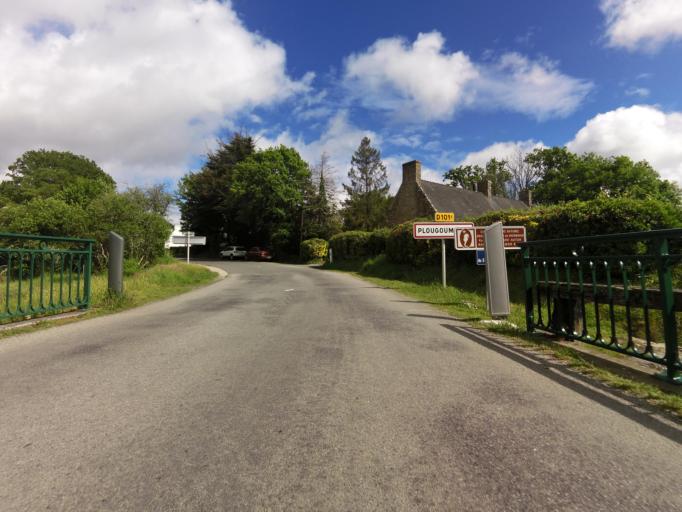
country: FR
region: Brittany
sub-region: Departement du Morbihan
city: Plougoumelen
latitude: 47.6496
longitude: -2.9302
